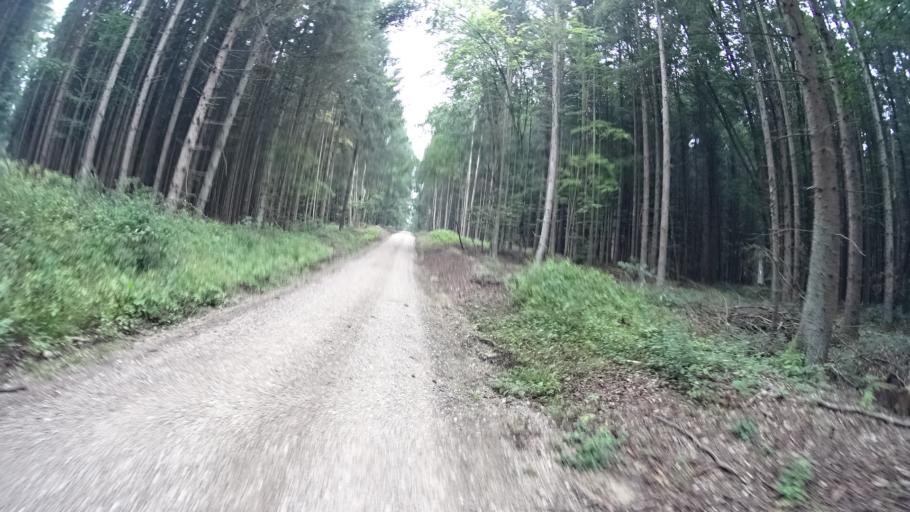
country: DE
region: Bavaria
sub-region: Upper Bavaria
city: Stammham
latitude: 48.8408
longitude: 11.4854
